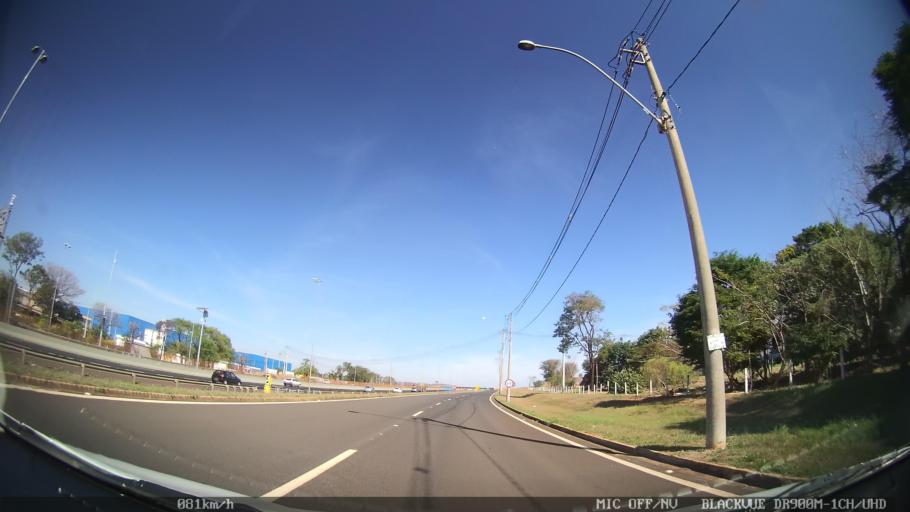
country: BR
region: Sao Paulo
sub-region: Ribeirao Preto
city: Ribeirao Preto
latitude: -21.1983
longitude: -47.7583
